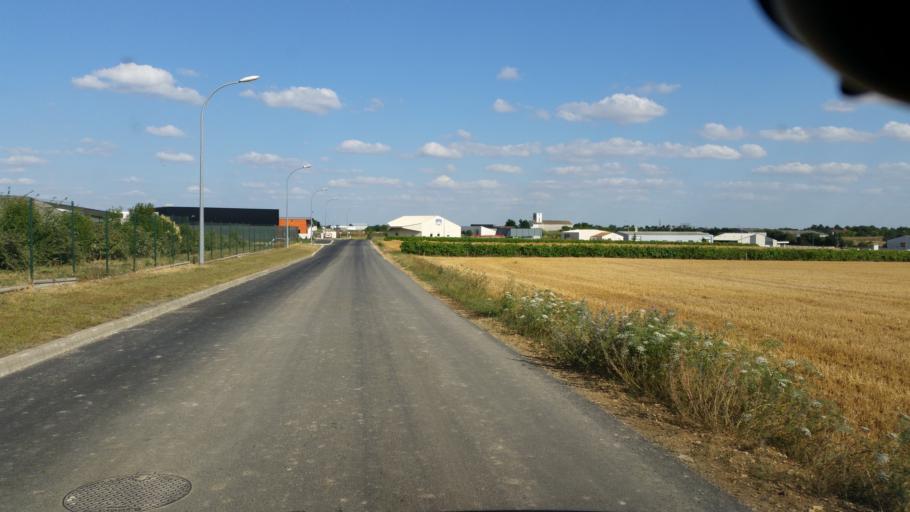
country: FR
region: Poitou-Charentes
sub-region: Departement de la Charente-Maritime
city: Saint-Jean-de-Liversay
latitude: 46.2331
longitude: -0.8870
